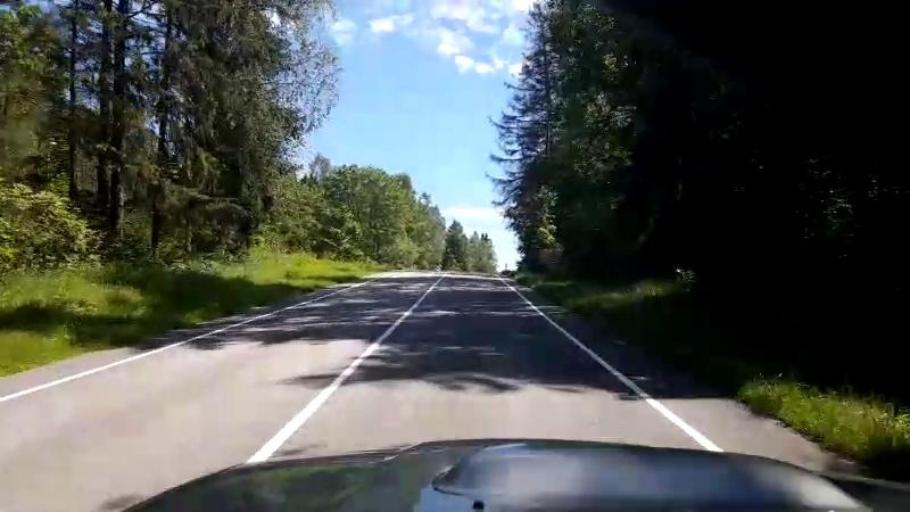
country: EE
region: Jaervamaa
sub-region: Jaerva-Jaani vald
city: Jarva-Jaani
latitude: 59.0302
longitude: 25.8941
